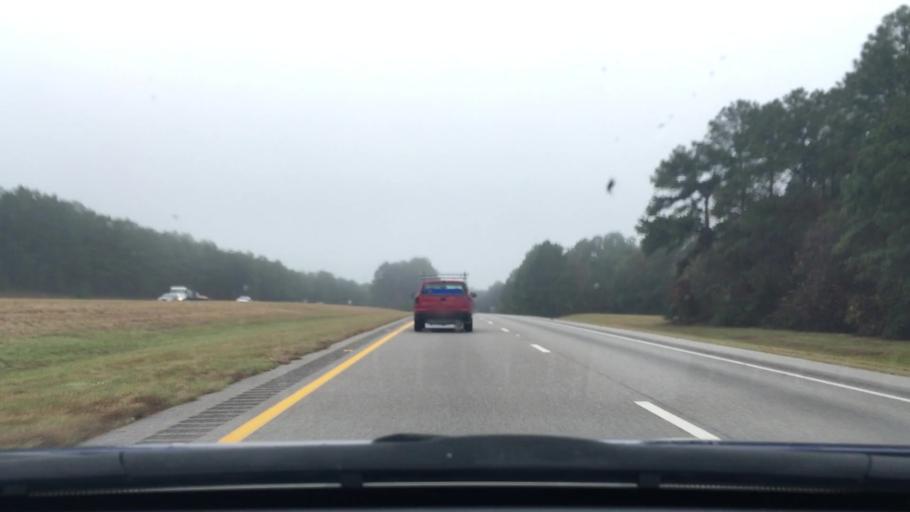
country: US
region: South Carolina
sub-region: Kershaw County
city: Camden
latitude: 34.2090
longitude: -80.4655
